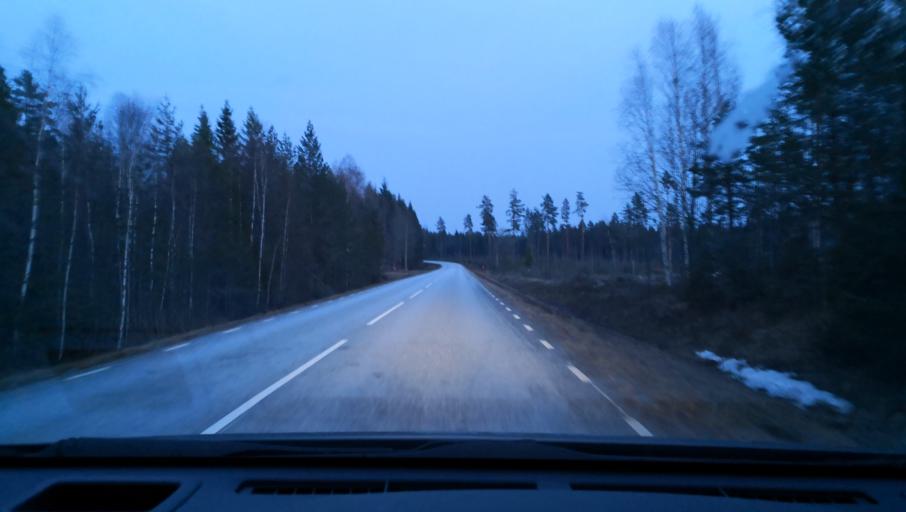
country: SE
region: OErebro
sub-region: Lindesbergs Kommun
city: Frovi
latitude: 59.5938
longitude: 15.3884
